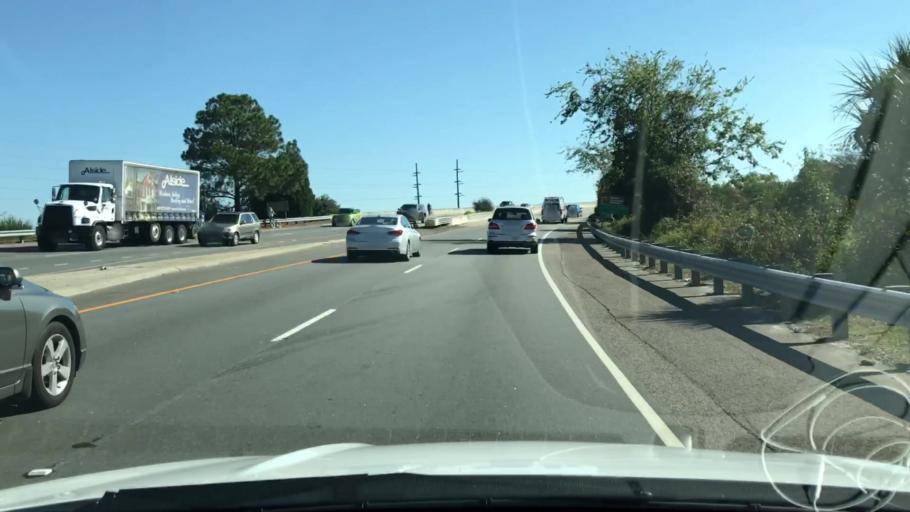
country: US
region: South Carolina
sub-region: Beaufort County
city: Hilton Head Island
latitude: 32.2282
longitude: -80.7855
